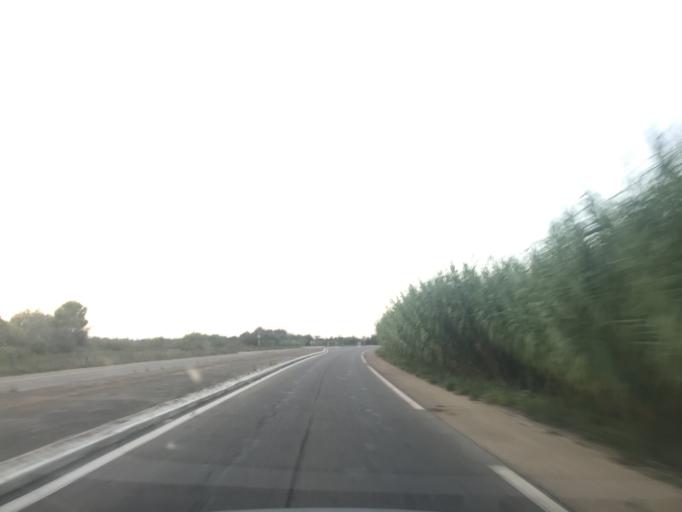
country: FR
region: Provence-Alpes-Cote d'Azur
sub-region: Departement des Bouches-du-Rhone
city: Saintes-Maries-de-la-Mer
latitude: 43.4803
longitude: 4.4055
